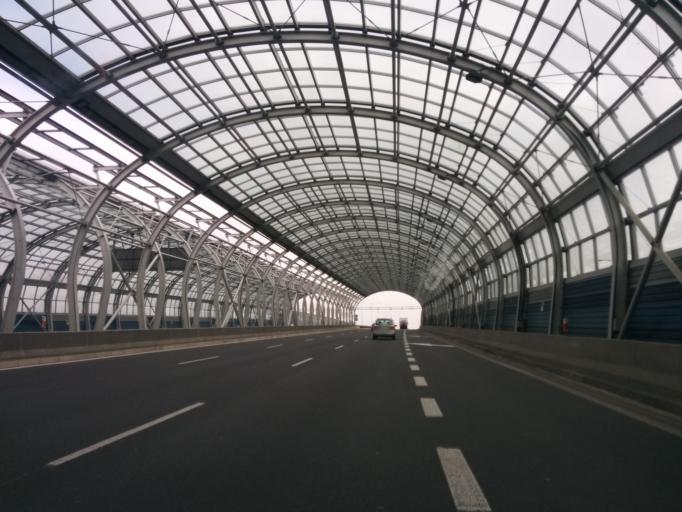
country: PL
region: Masovian Voivodeship
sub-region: Warszawa
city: Targowek
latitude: 52.2985
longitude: 21.0295
